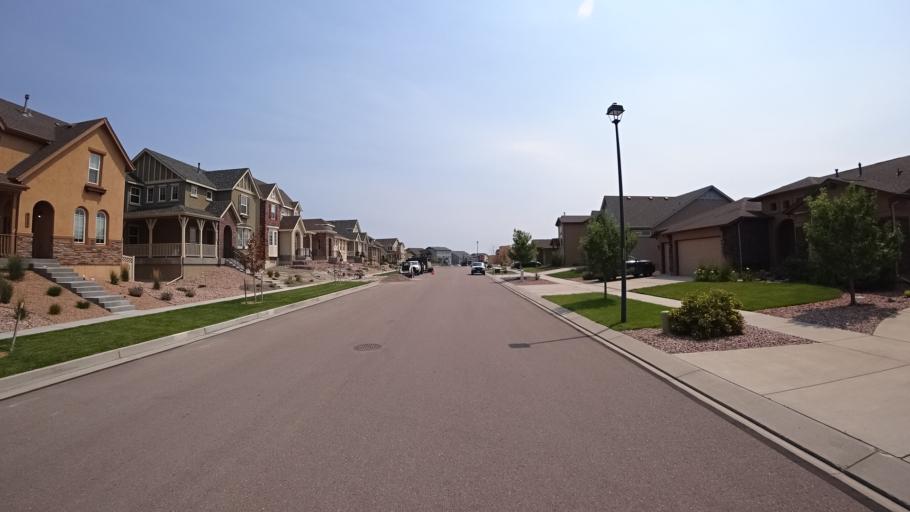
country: US
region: Colorado
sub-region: El Paso County
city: Black Forest
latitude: 38.9698
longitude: -104.7171
